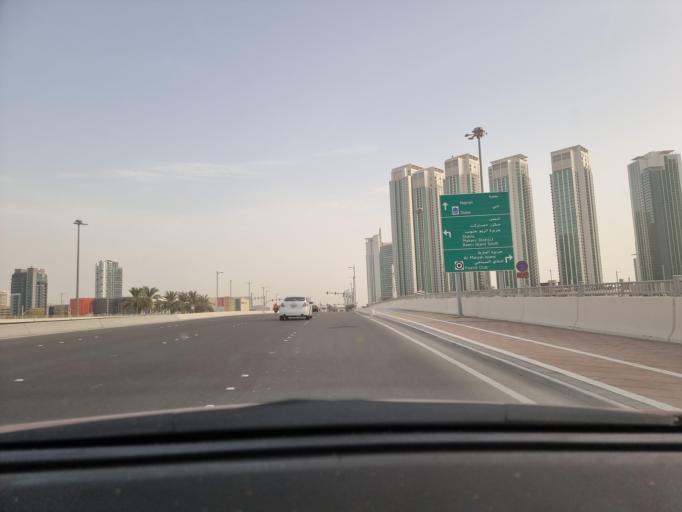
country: AE
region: Abu Dhabi
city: Abu Dhabi
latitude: 24.4962
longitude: 54.3972
